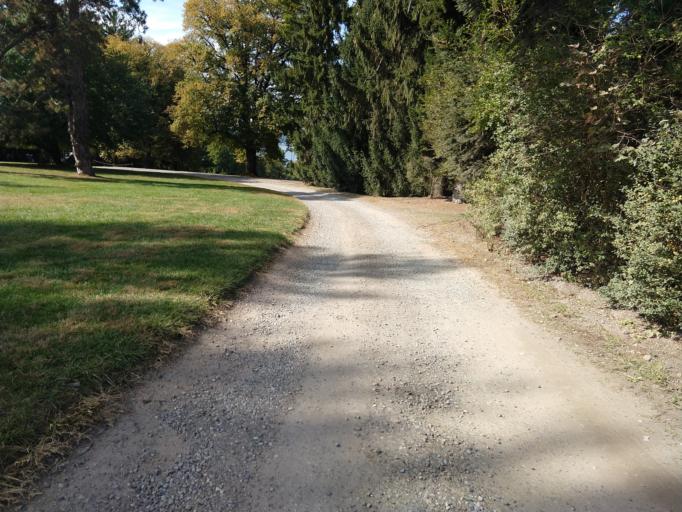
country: US
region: New York
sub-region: Westchester County
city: Irvington
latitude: 41.0554
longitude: -73.8658
